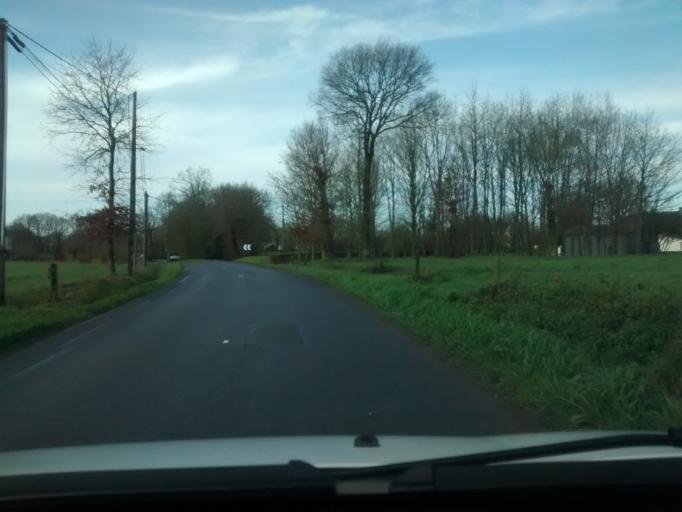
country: FR
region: Brittany
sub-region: Departement d'Ille-et-Vilaine
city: Pace
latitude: 48.1464
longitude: -1.7457
